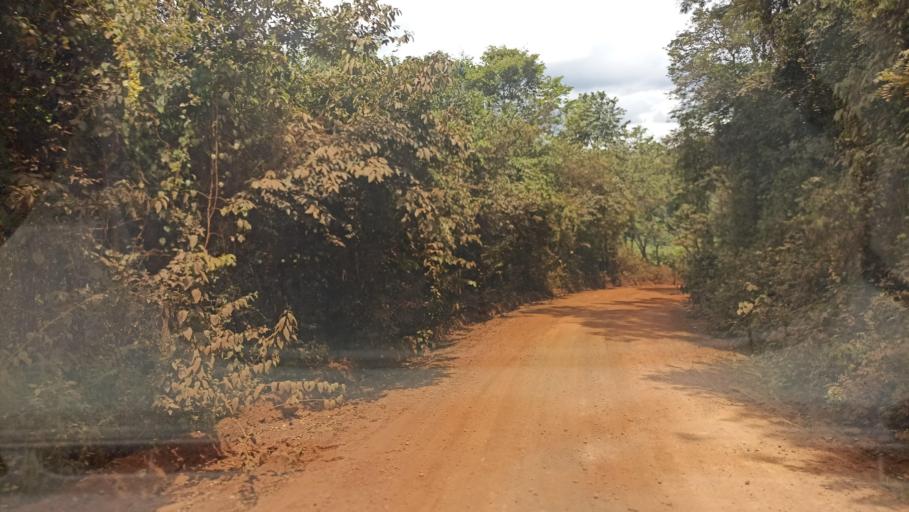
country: BR
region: Minas Gerais
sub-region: Itabirito
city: Itabirito
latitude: -20.3360
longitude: -43.7645
